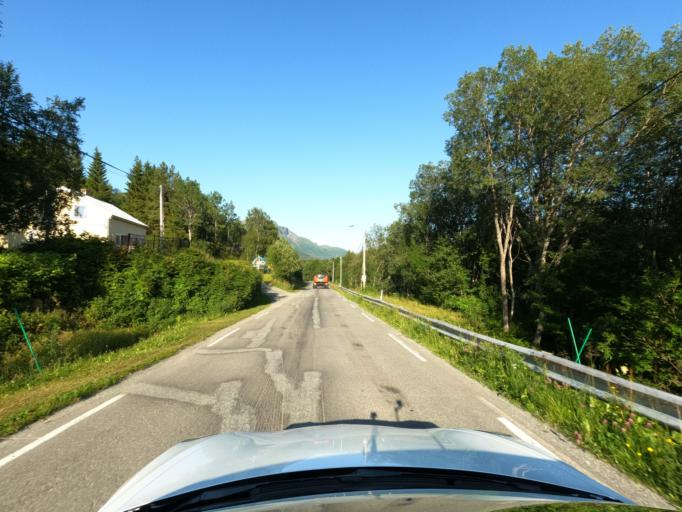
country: NO
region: Nordland
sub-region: Narvik
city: Bjerkvik
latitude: 68.5543
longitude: 17.5978
